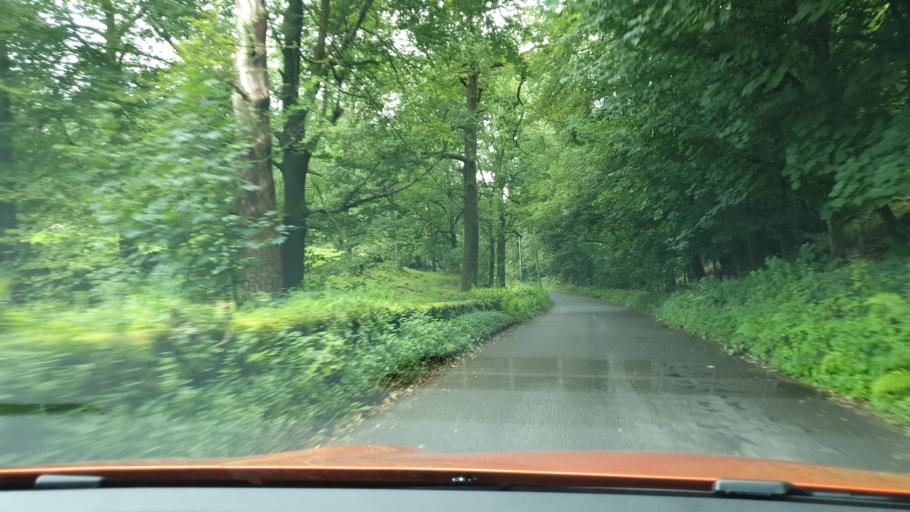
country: GB
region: England
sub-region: Cumbria
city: Grange-over-Sands
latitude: 54.2712
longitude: -2.9866
